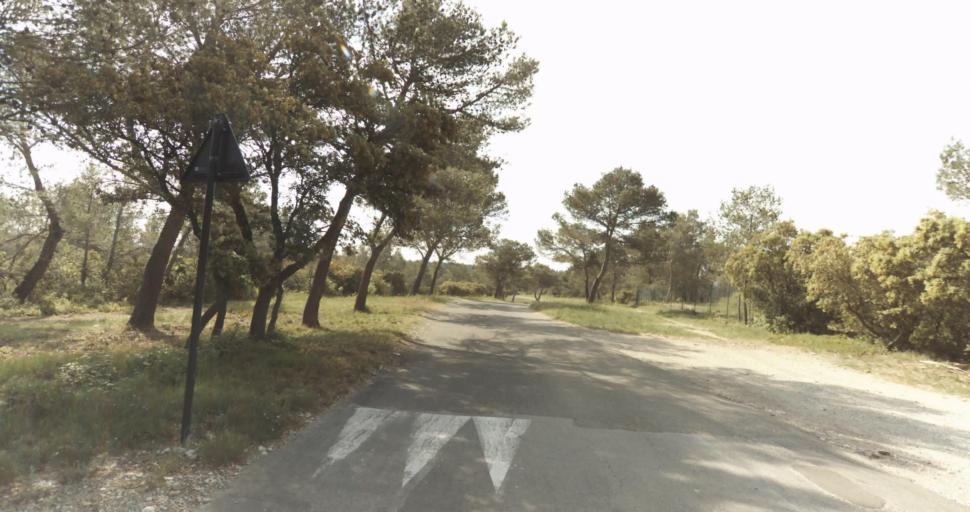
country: FR
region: Languedoc-Roussillon
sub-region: Departement du Gard
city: Poulx
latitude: 43.8786
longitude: 4.3903
